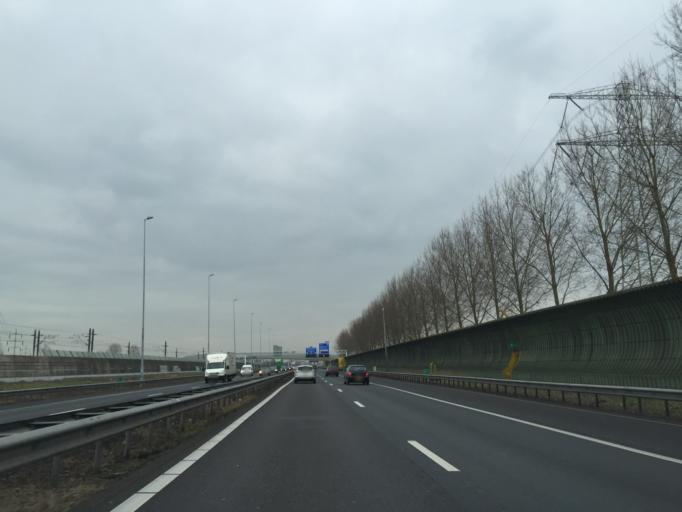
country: NL
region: South Holland
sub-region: Gemeente Papendrecht
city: Papendrecht
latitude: 51.8361
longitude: 4.7255
